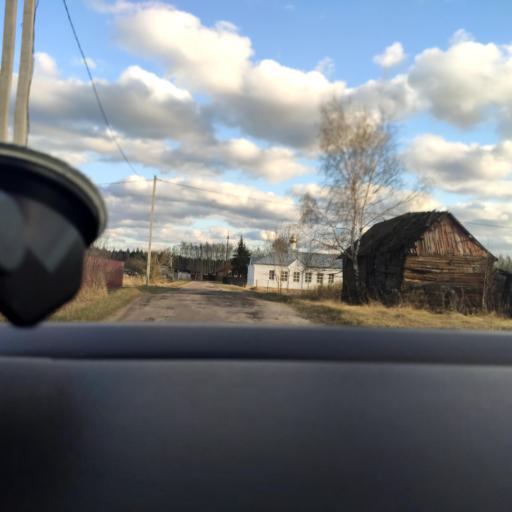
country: RU
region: Moskovskaya
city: Shaturtorf
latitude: 55.4347
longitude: 39.4273
